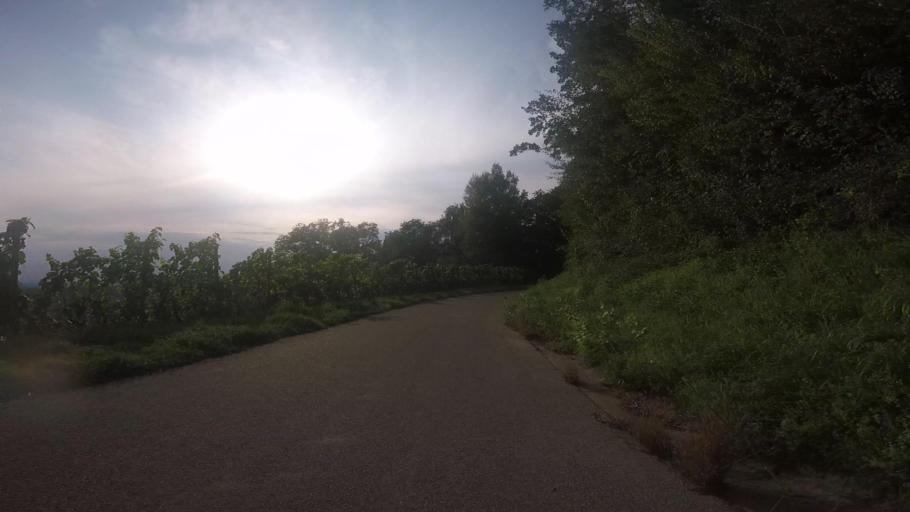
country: DE
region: Baden-Wuerttemberg
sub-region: Regierungsbezirk Stuttgart
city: Aspach
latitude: 49.0006
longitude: 9.3689
